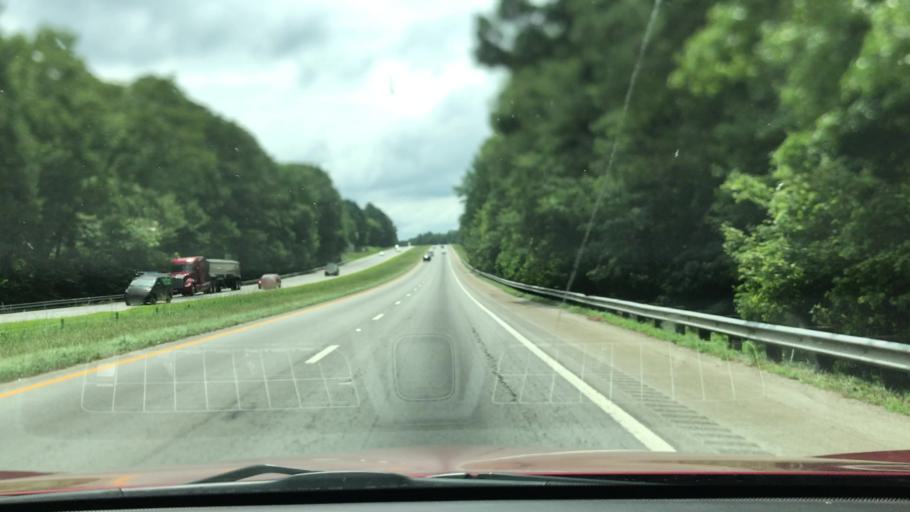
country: US
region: South Carolina
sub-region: Newberry County
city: Newberry
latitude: 34.3682
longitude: -81.6697
